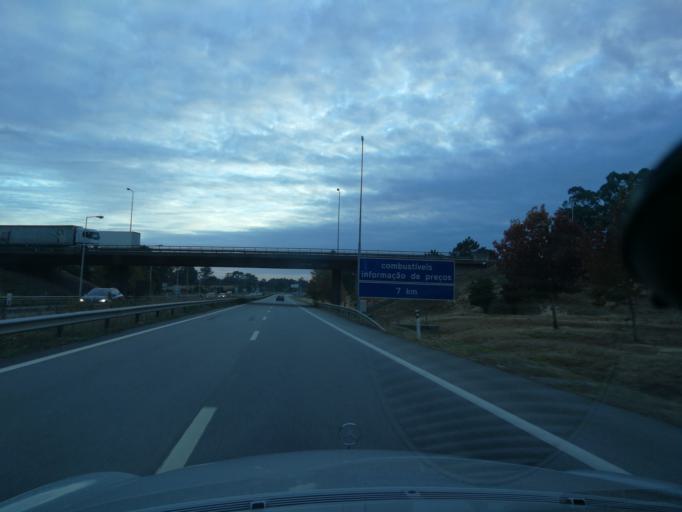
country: PT
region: Aveiro
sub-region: Albergaria-A-Velha
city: Albergaria-a-Velha
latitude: 40.6864
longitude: -8.5243
